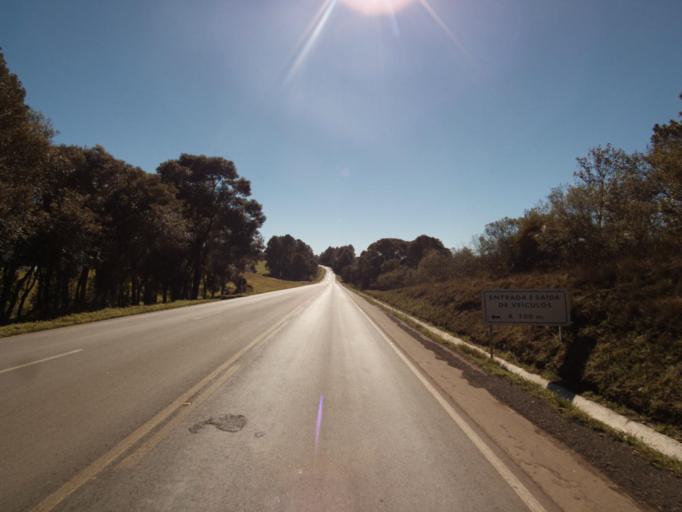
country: BR
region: Santa Catarina
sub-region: Concordia
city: Concordia
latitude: -26.9578
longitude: -51.8553
